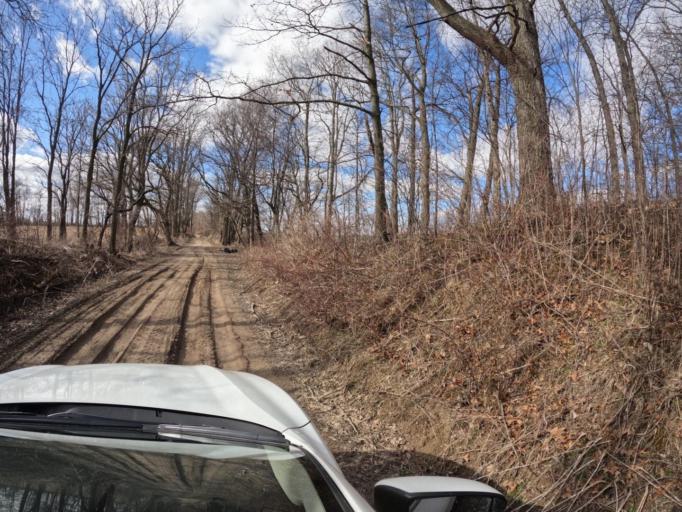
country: CA
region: Ontario
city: Norfolk County
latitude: 42.7588
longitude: -80.3148
